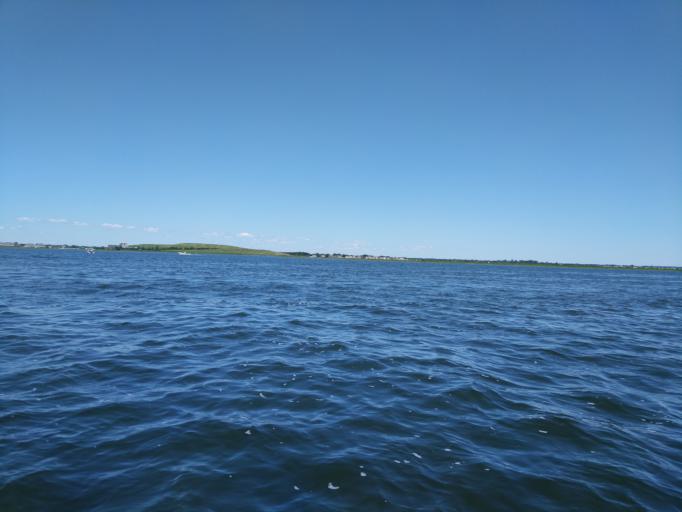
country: US
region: New York
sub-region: Nassau County
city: Barnum Island
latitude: 40.5962
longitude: -73.6354
